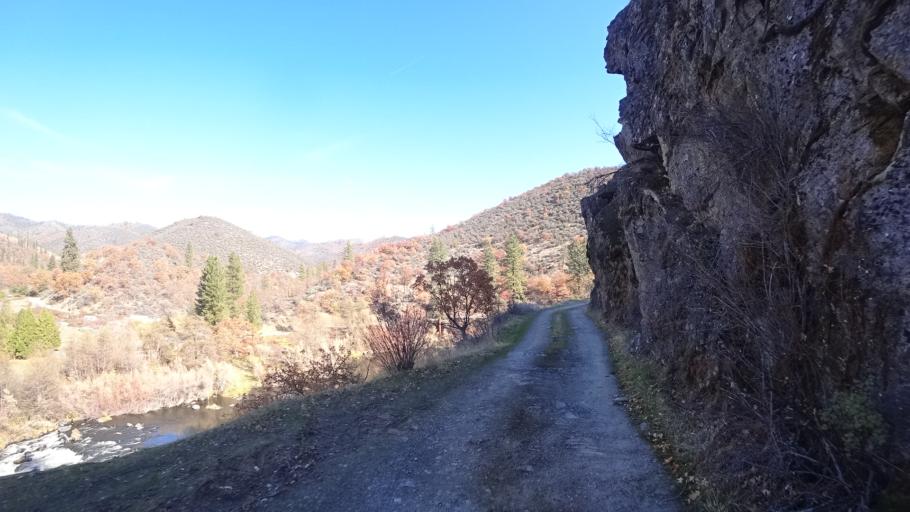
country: US
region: California
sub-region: Siskiyou County
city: Yreka
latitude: 41.8662
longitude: -122.7382
